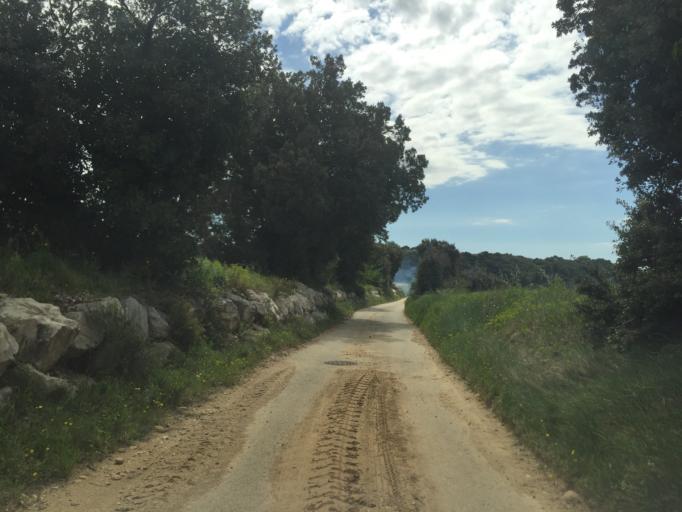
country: FR
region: Provence-Alpes-Cote d'Azur
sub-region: Departement du Vaucluse
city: Chateauneuf-du-Pape
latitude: 44.0747
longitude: 4.8260
